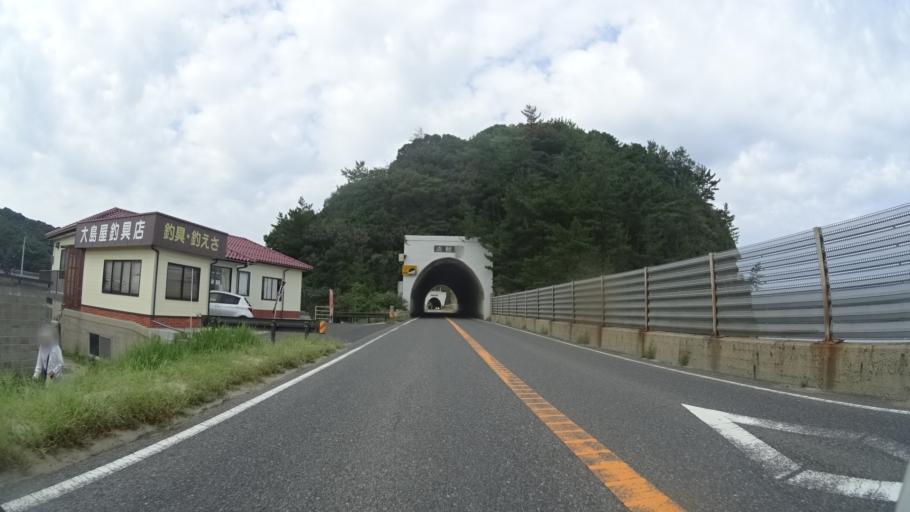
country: JP
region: Shimane
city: Odacho-oda
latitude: 35.1947
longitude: 132.4425
